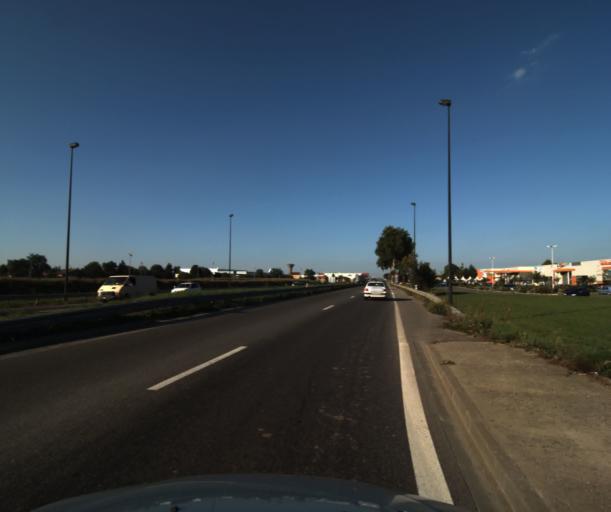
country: FR
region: Midi-Pyrenees
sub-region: Departement de la Haute-Garonne
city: Roquettes
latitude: 43.5060
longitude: 1.3621
